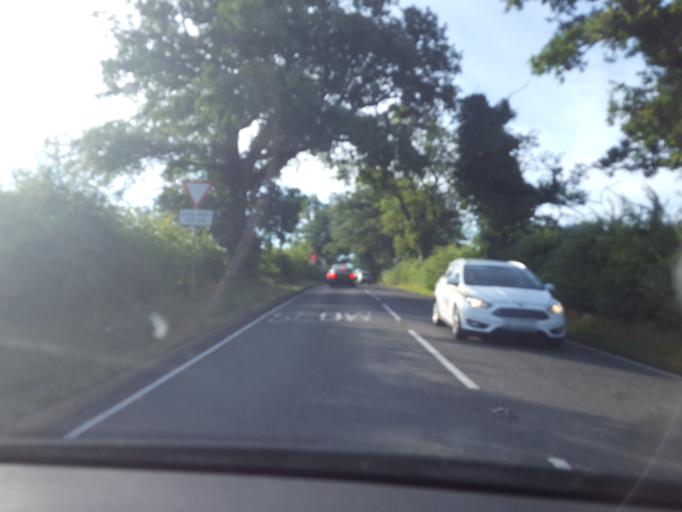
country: GB
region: England
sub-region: Leicestershire
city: Shepshed
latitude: 52.7417
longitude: -1.2701
